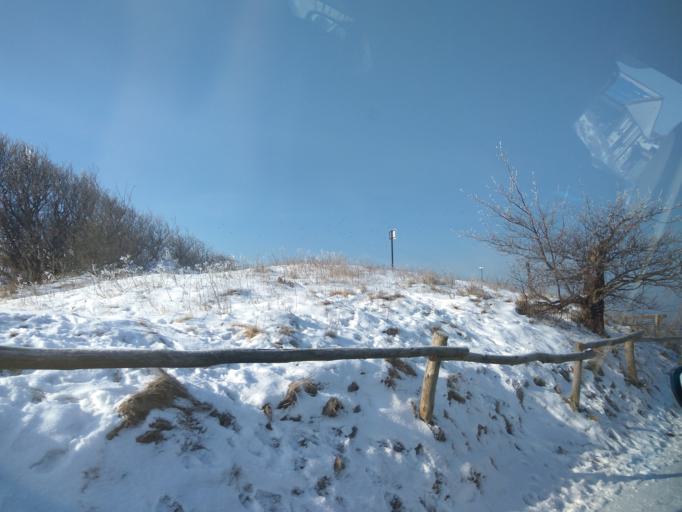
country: RU
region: Kaliningrad
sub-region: Zelenogradskiy Rayon
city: Zelenogradsk
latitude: 55.0166
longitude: 20.6121
